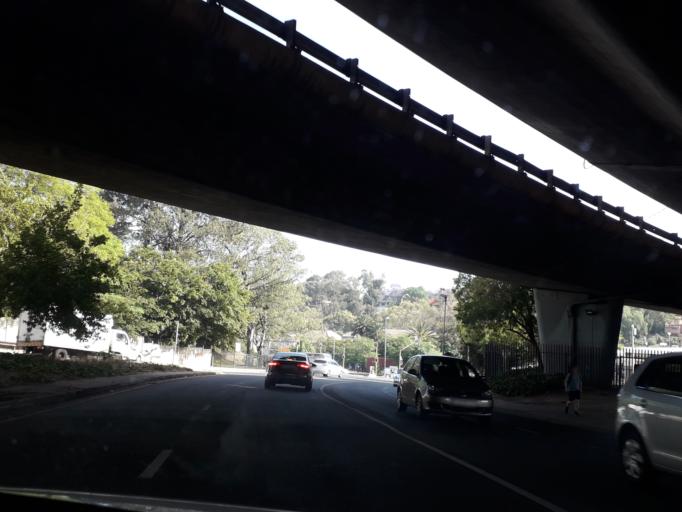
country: ZA
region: Gauteng
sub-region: City of Johannesburg Metropolitan Municipality
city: Johannesburg
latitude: -26.1863
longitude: 28.0277
